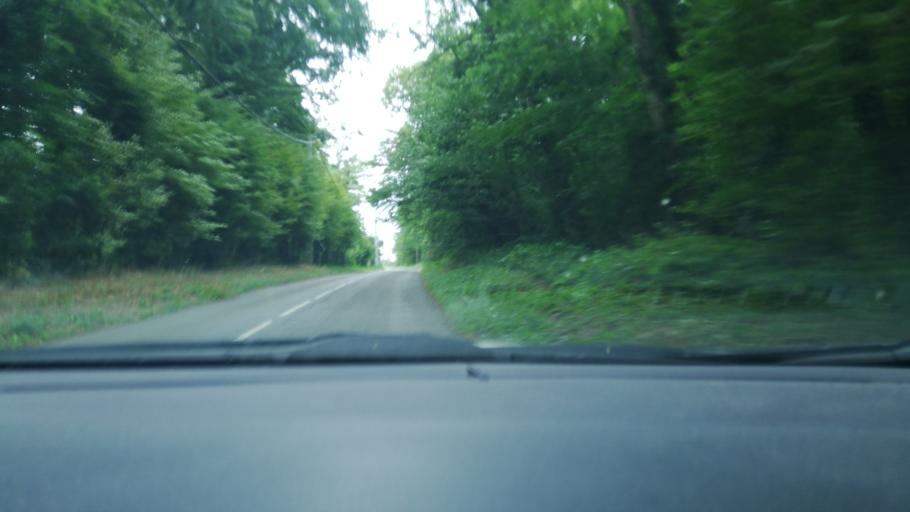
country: FR
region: Ile-de-France
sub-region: Departement du Val-d'Oise
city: Ennery
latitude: 49.0931
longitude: 2.0841
